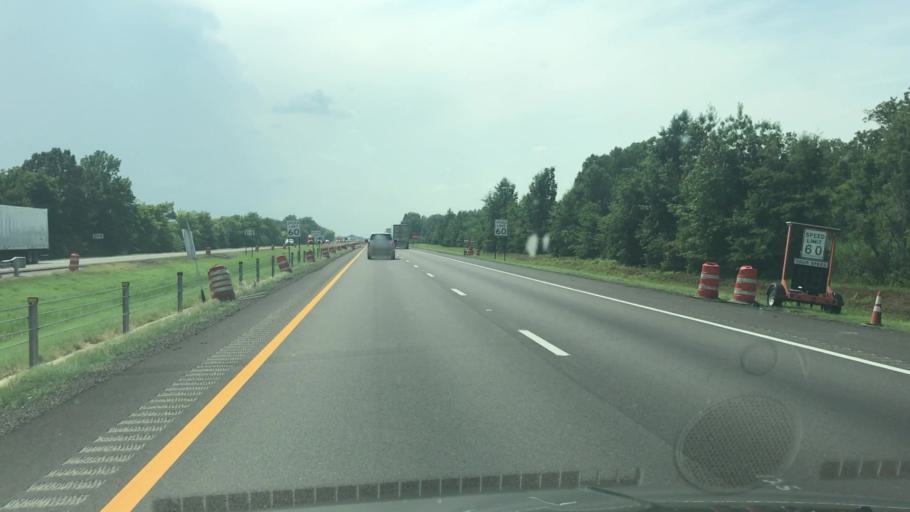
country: US
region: Arkansas
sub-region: Crittenden County
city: Earle
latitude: 35.1341
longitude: -90.4454
